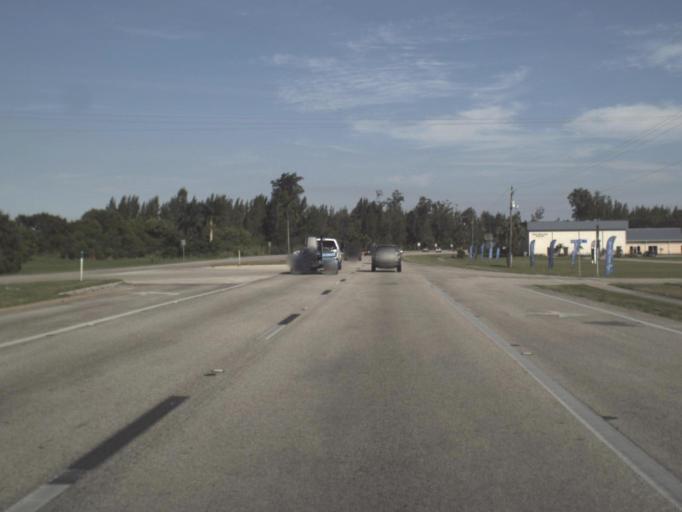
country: US
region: Florida
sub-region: Hendry County
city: Clewiston
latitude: 26.7542
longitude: -80.9142
